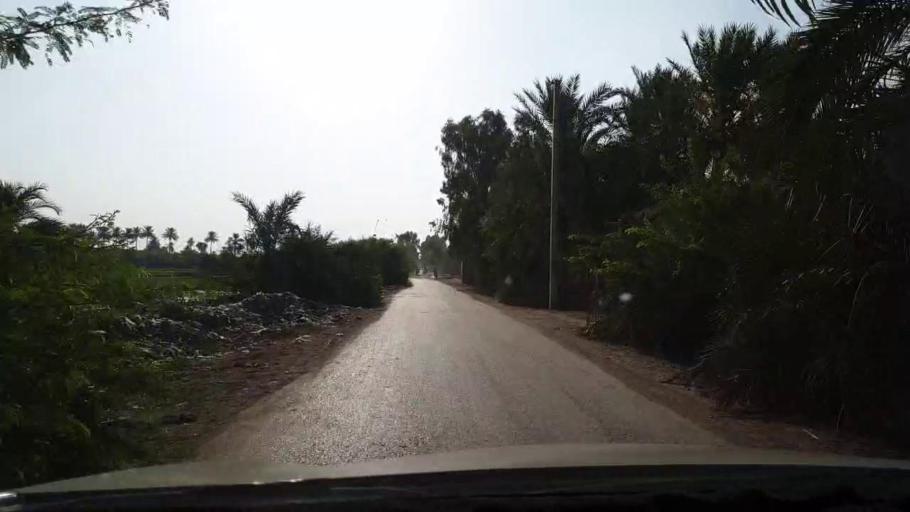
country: PK
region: Sindh
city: Larkana
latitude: 27.5506
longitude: 68.2385
